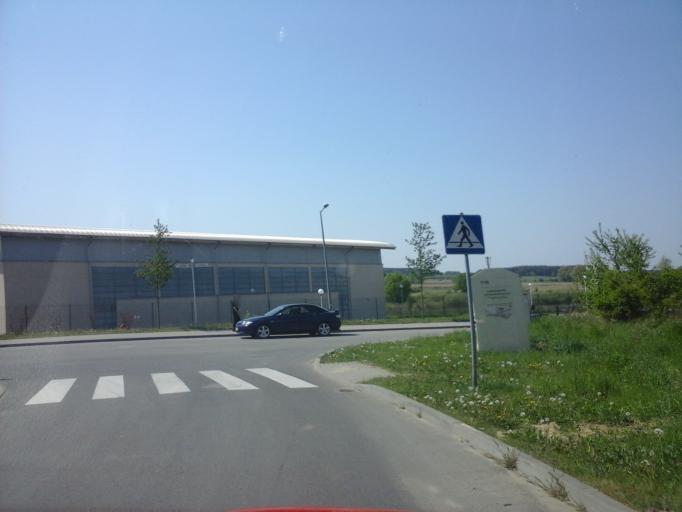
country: PL
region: West Pomeranian Voivodeship
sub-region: Powiat choszczenski
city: Choszczno
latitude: 53.1754
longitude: 15.4067
